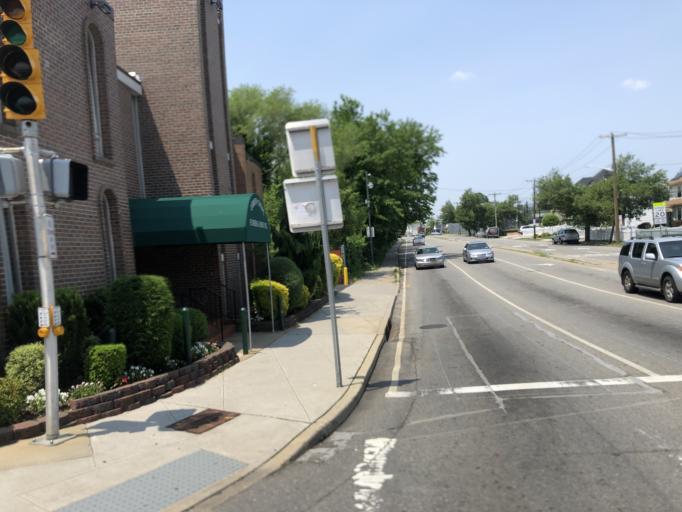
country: US
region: New York
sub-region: Nassau County
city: Elmont
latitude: 40.6942
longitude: -73.7177
